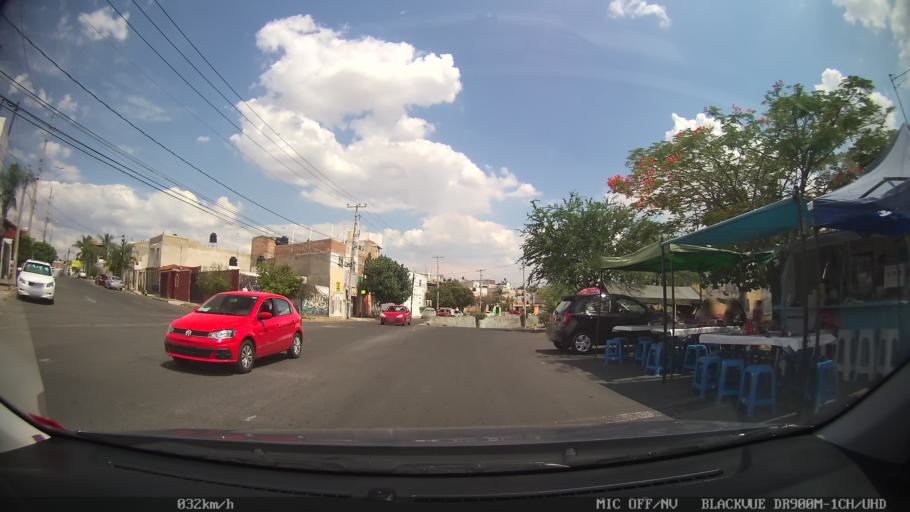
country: MX
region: Jalisco
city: Tonala
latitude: 20.6253
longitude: -103.2518
